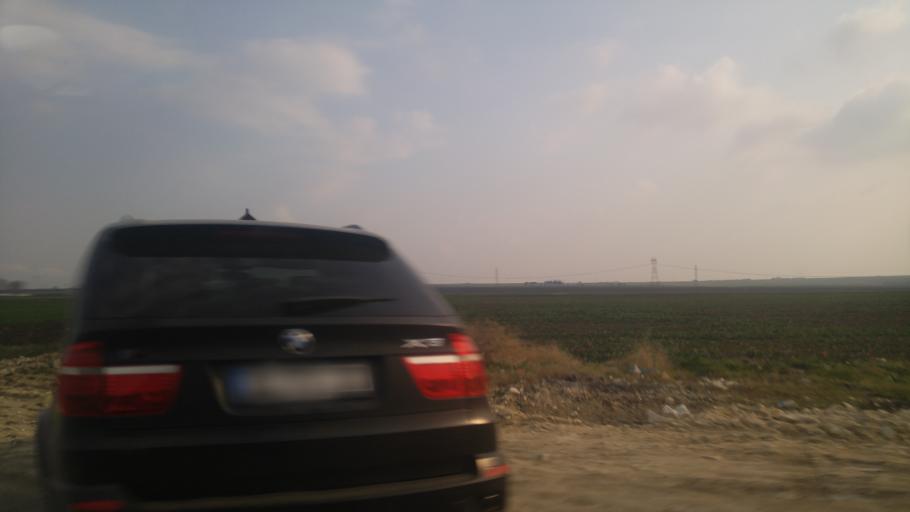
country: TR
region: Istanbul
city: Kavakli
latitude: 41.1051
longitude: 28.2894
